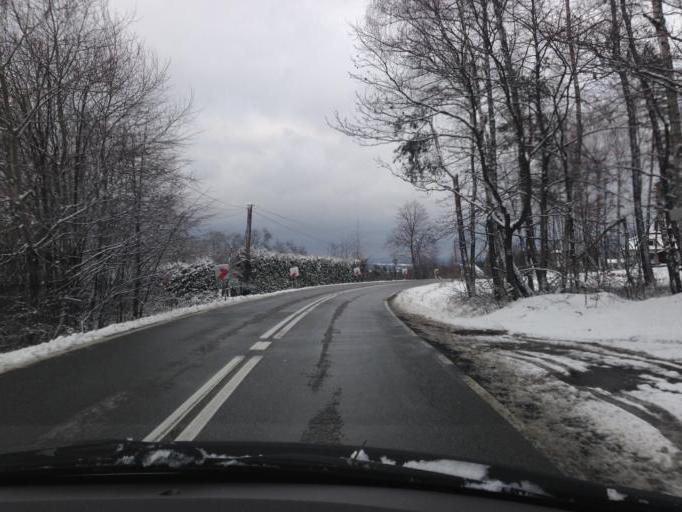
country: PL
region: Lesser Poland Voivodeship
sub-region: Powiat bochenski
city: Nowy Wisnicz
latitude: 49.8523
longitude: 20.4771
